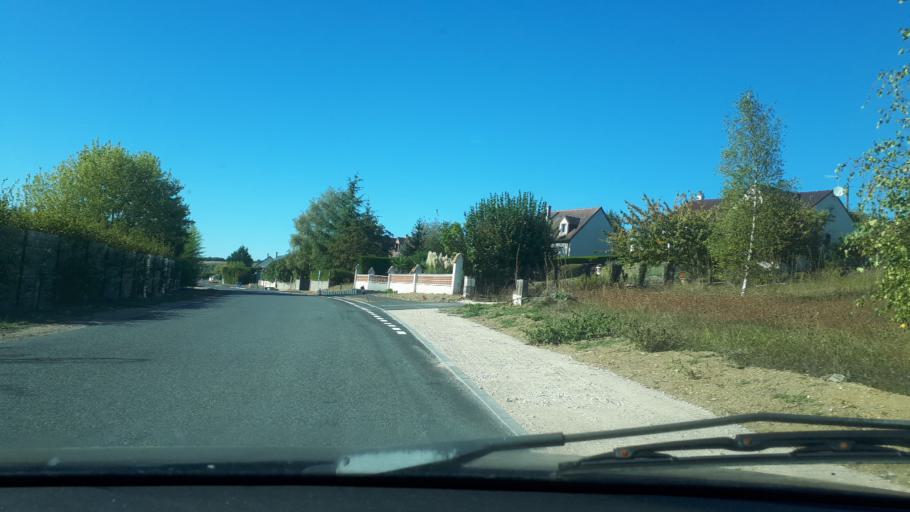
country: FR
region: Centre
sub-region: Departement du Loir-et-Cher
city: Villiers-sur-Loir
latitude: 47.7999
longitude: 1.0031
